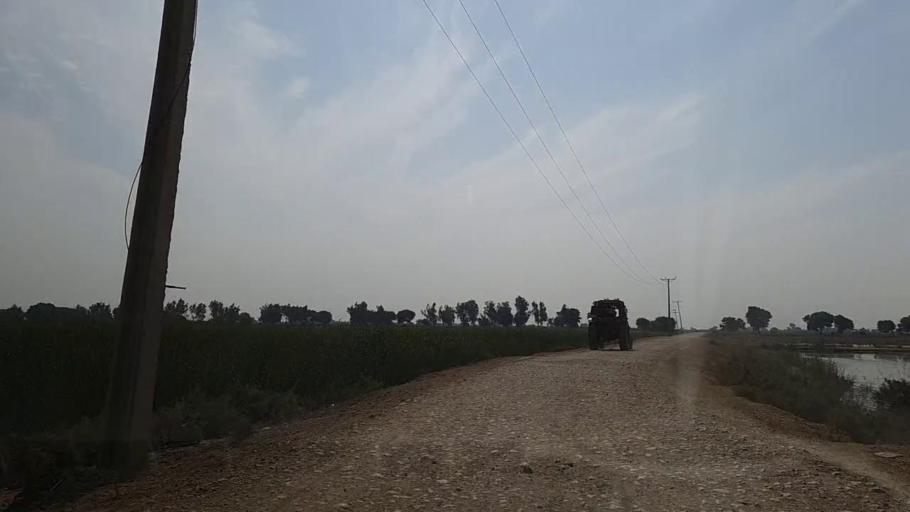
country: PK
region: Sindh
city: Mirpur Batoro
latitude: 24.6137
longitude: 68.2364
